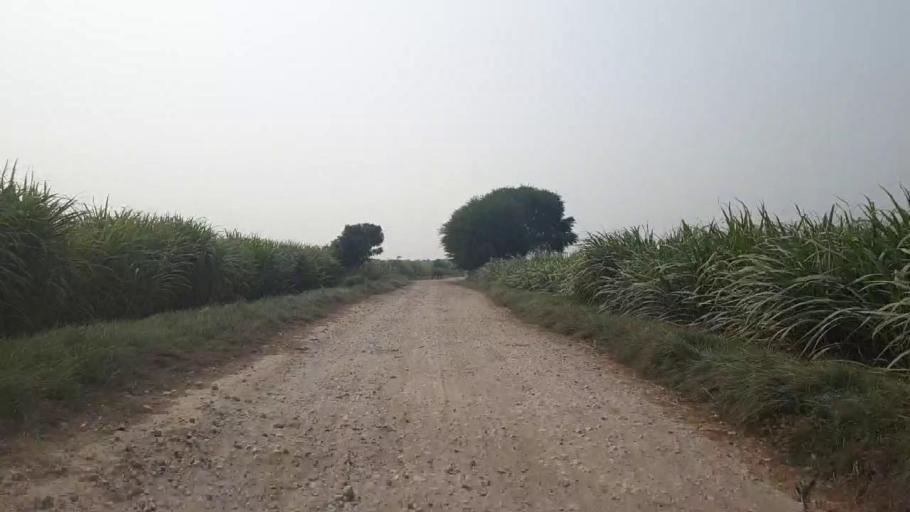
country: PK
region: Sindh
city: Tando Muhammad Khan
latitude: 25.2290
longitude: 68.5660
